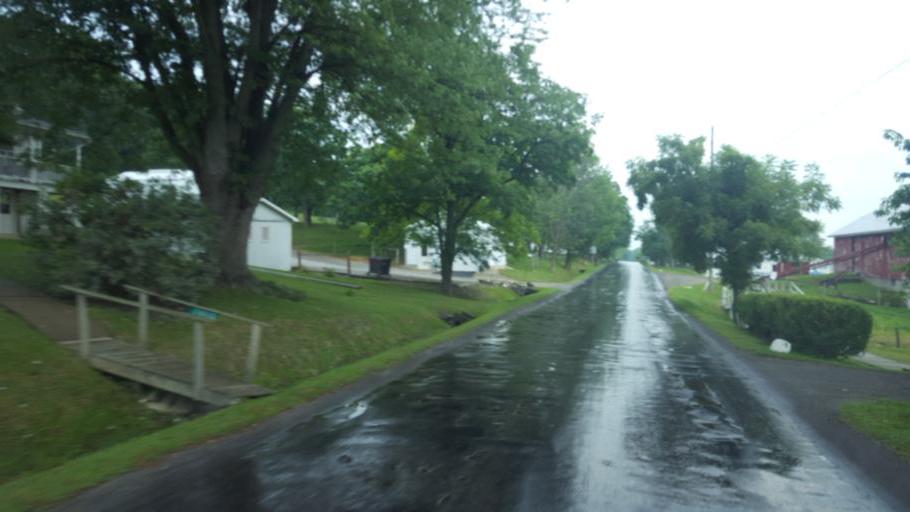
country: US
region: Ohio
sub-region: Geauga County
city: Middlefield
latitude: 41.4382
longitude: -80.9952
